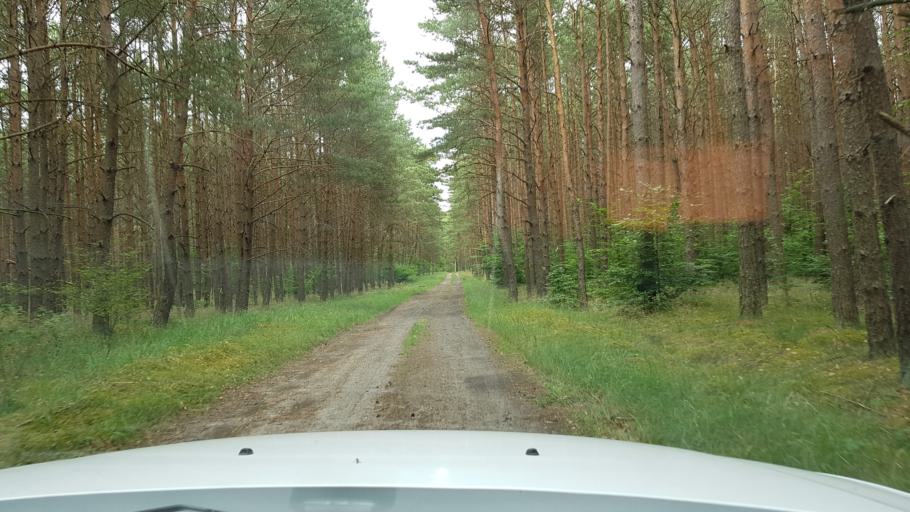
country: PL
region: West Pomeranian Voivodeship
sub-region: Powiat mysliborski
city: Boleszkowice
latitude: 52.6562
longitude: 14.5674
